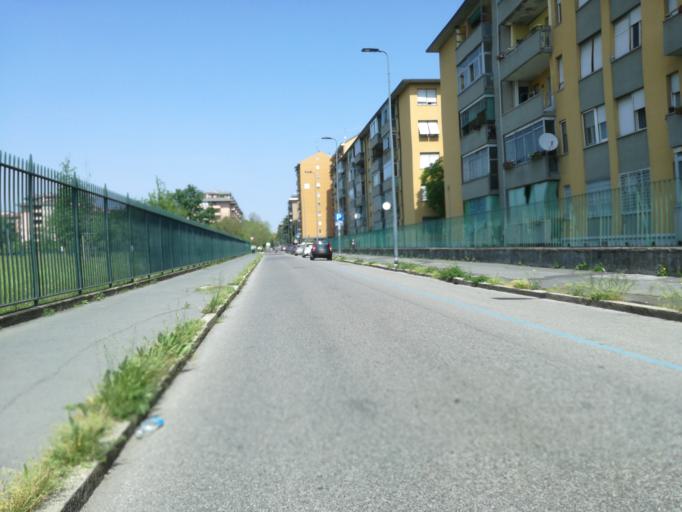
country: IT
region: Lombardy
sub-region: Citta metropolitana di Milano
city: Romano Banco
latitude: 45.4517
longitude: 9.1237
